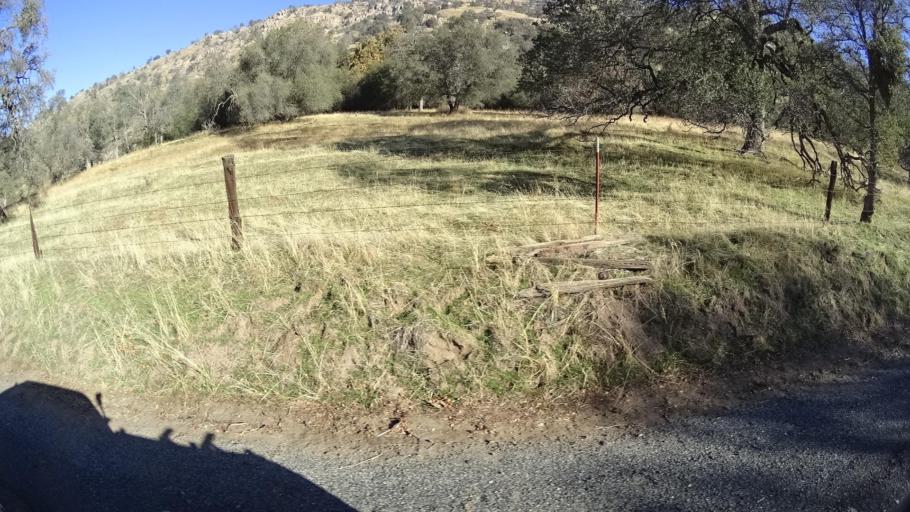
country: US
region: California
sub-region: Kern County
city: Alta Sierra
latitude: 35.7868
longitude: -118.7890
